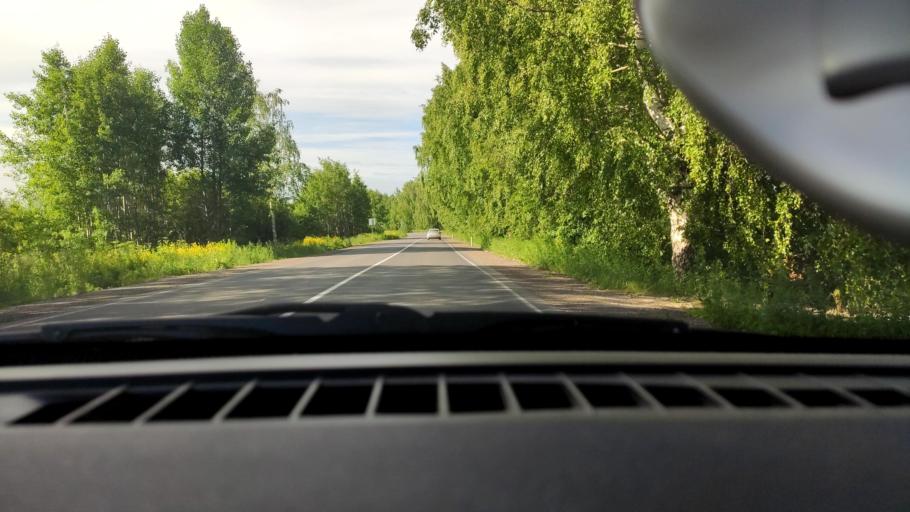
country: RU
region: Perm
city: Nytva
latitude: 57.9310
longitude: 55.4515
